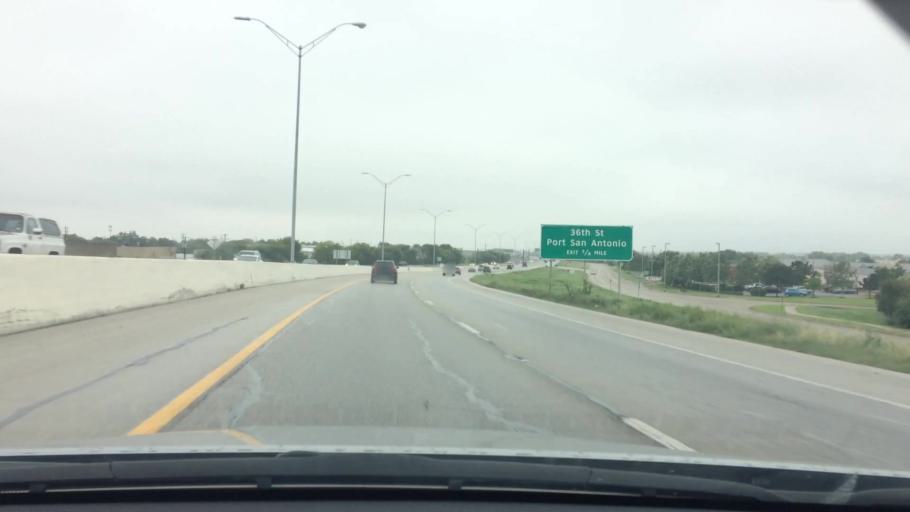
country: US
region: Texas
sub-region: Bexar County
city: Lackland Air Force Base
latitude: 29.4173
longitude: -98.5899
